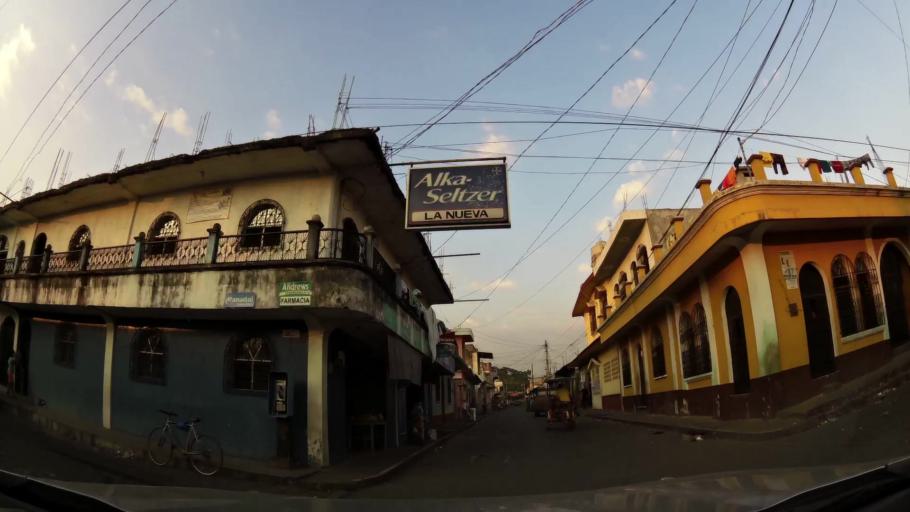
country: GT
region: Retalhuleu
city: San Sebastian
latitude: 14.5621
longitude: -91.6494
